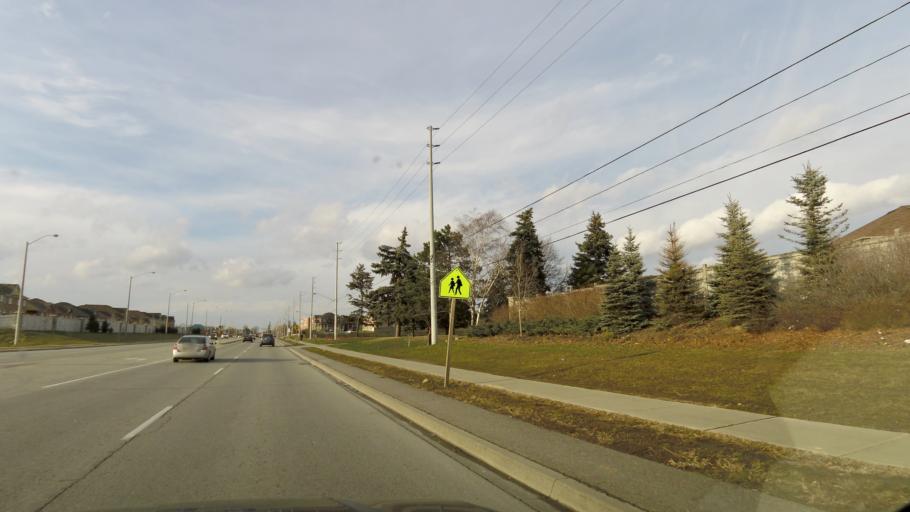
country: CA
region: Ontario
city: Brampton
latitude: 43.7809
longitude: -79.6748
